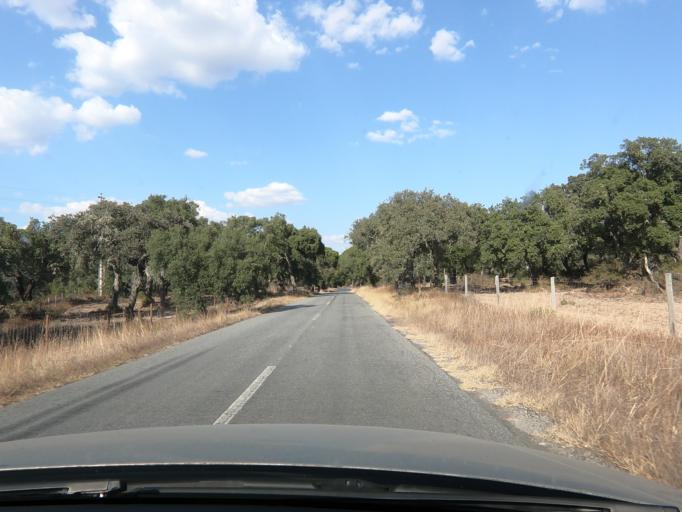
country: PT
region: Setubal
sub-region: Alcacer do Sal
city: Alcacer do Sal
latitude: 38.2605
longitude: -8.3539
